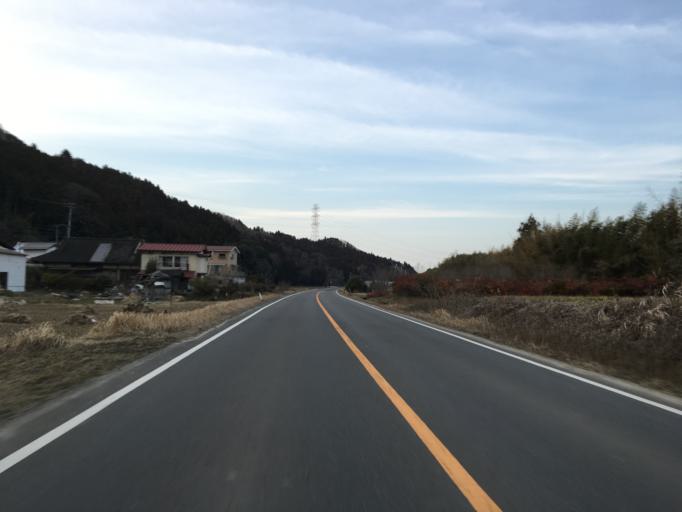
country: JP
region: Ibaraki
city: Daigo
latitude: 36.8842
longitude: 140.4127
